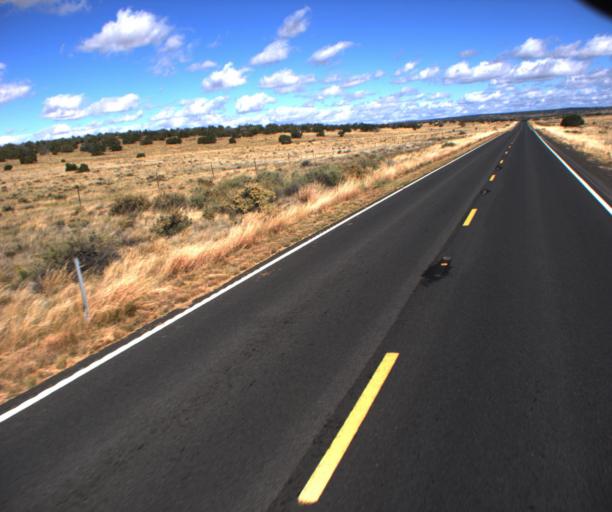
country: US
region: Arizona
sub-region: Apache County
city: Houck
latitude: 34.9893
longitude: -109.2271
